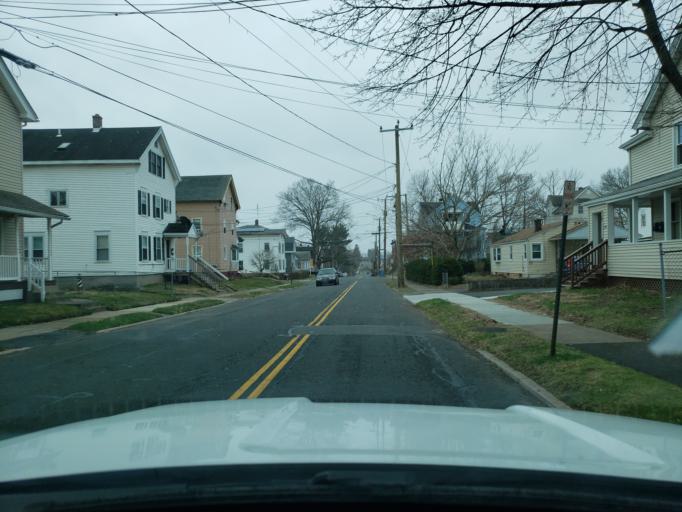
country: US
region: Connecticut
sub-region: Hartford County
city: New Britain
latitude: 41.6707
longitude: -72.7610
